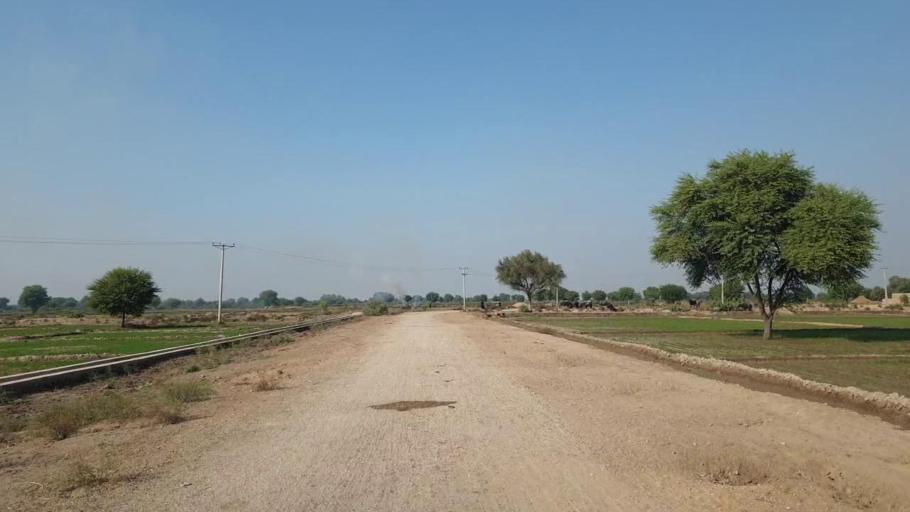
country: PK
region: Sindh
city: Sehwan
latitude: 26.4536
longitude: 67.8155
